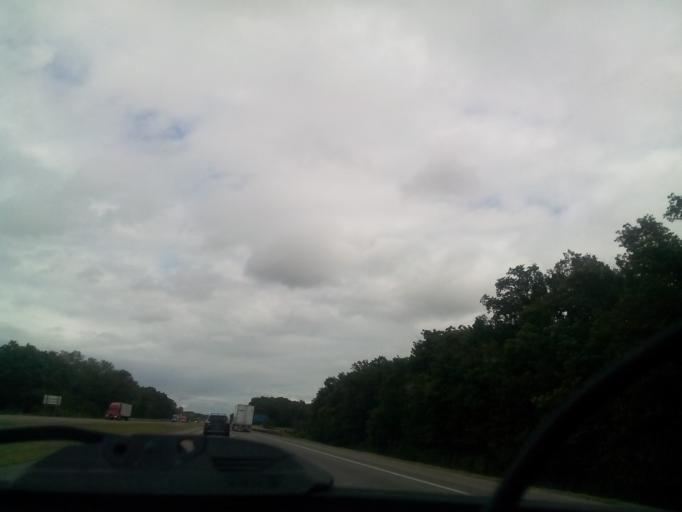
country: US
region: Ohio
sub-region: Williams County
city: Montpelier
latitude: 41.6285
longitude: -84.7408
